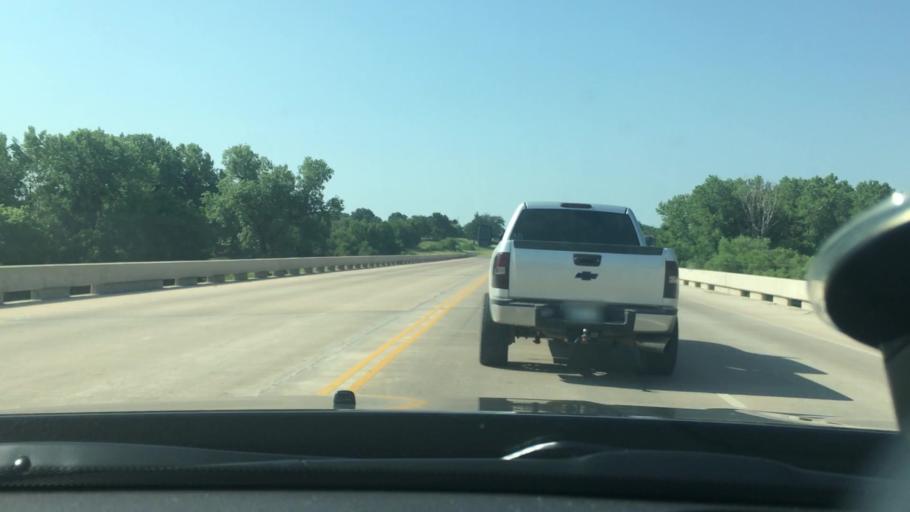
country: US
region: Oklahoma
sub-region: Garvin County
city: Lindsay
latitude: 34.8190
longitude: -97.5983
